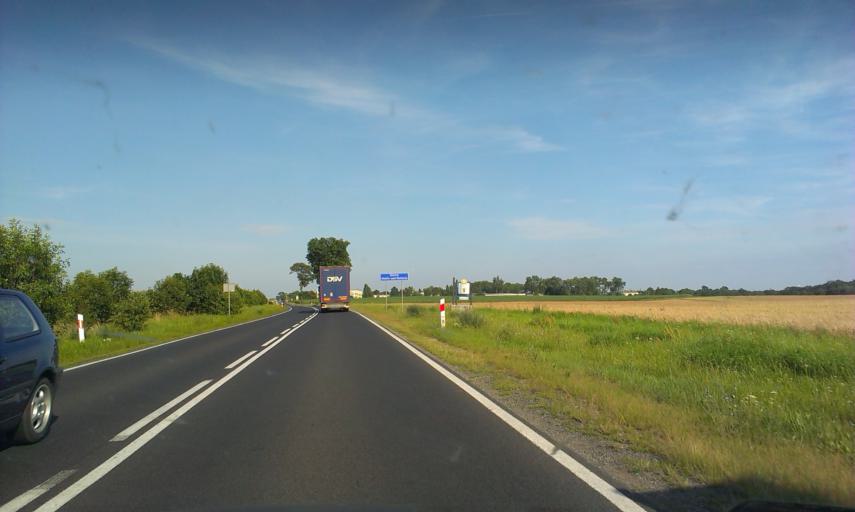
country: PL
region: Kujawsko-Pomorskie
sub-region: Powiat nakielski
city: Sadki
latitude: 53.1485
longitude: 17.5151
